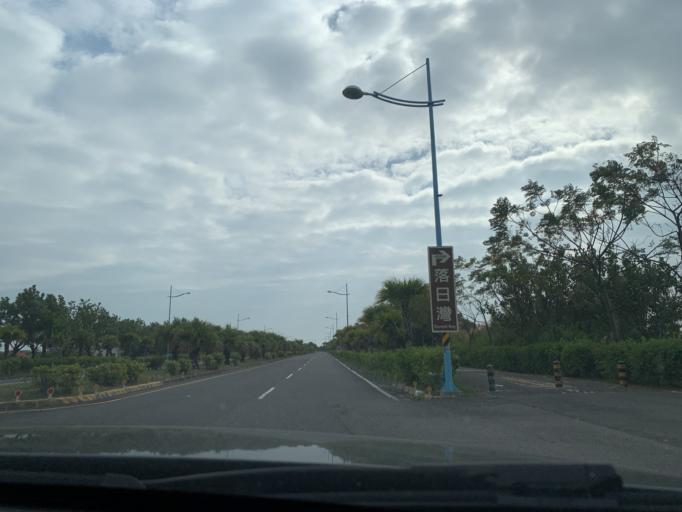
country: TW
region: Taiwan
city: Fengshan
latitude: 22.4488
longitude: 120.4877
